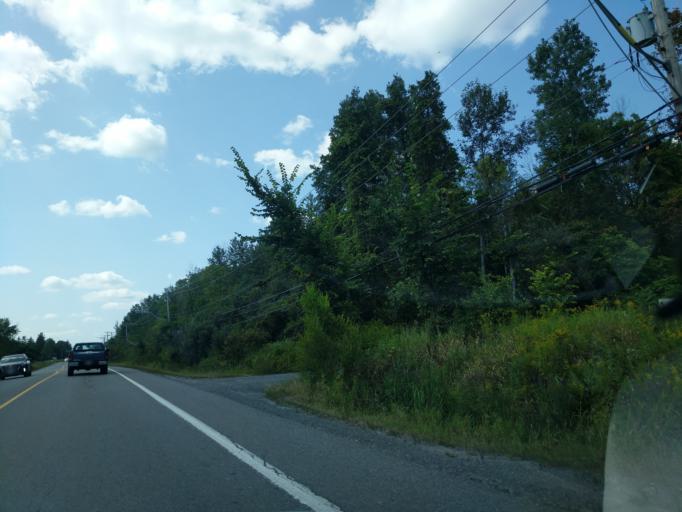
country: CA
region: Quebec
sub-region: Outaouais
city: Gatineau
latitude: 45.4425
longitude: -75.8073
